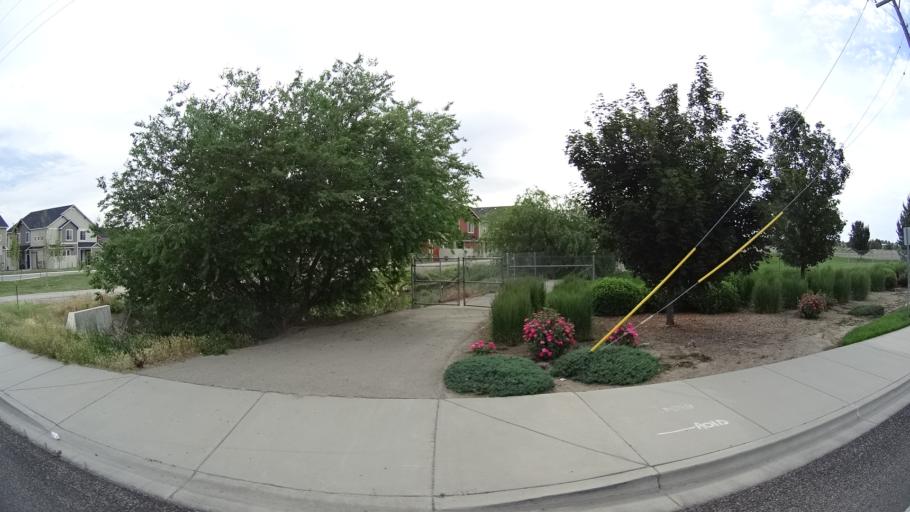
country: US
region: Idaho
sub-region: Ada County
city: Meridian
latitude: 43.6168
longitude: -116.3744
